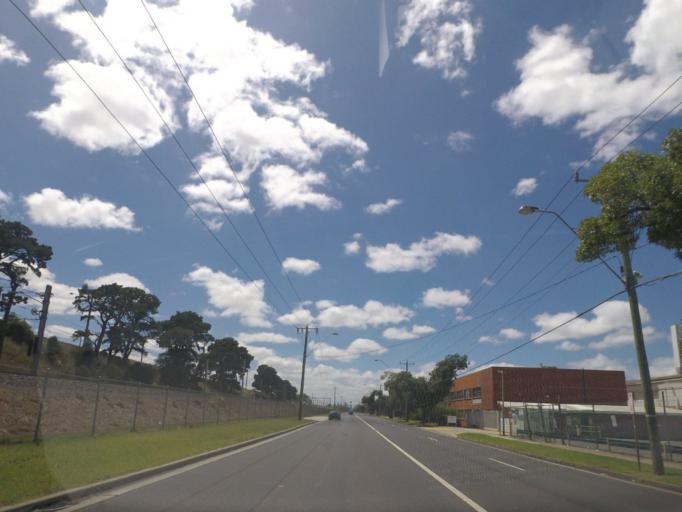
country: AU
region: Victoria
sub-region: Maribyrnong
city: Braybrook
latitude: -37.7986
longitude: 144.8549
